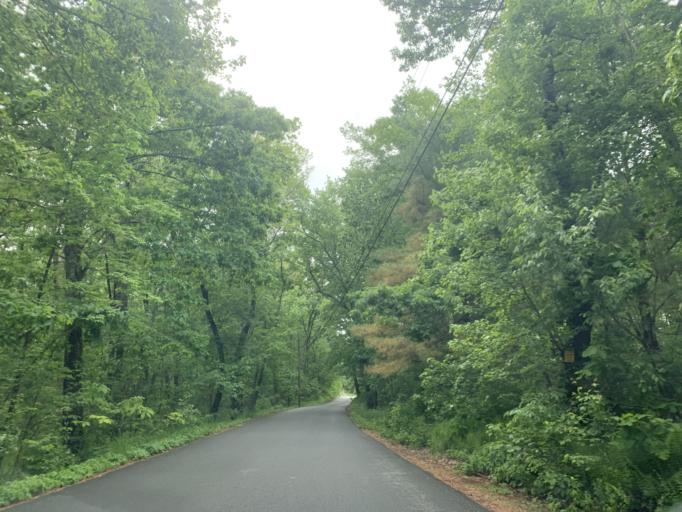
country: US
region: Massachusetts
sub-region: Worcester County
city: Grafton
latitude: 42.2016
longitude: -71.6563
